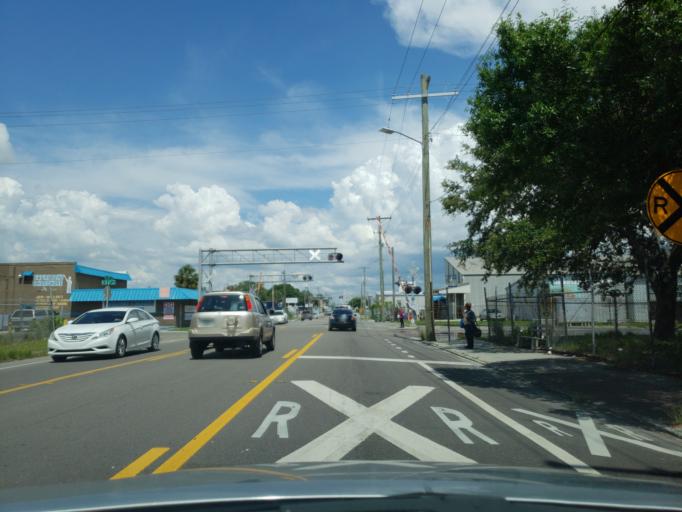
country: US
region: Florida
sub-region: Hillsborough County
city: Tampa
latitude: 27.9602
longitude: -82.4198
